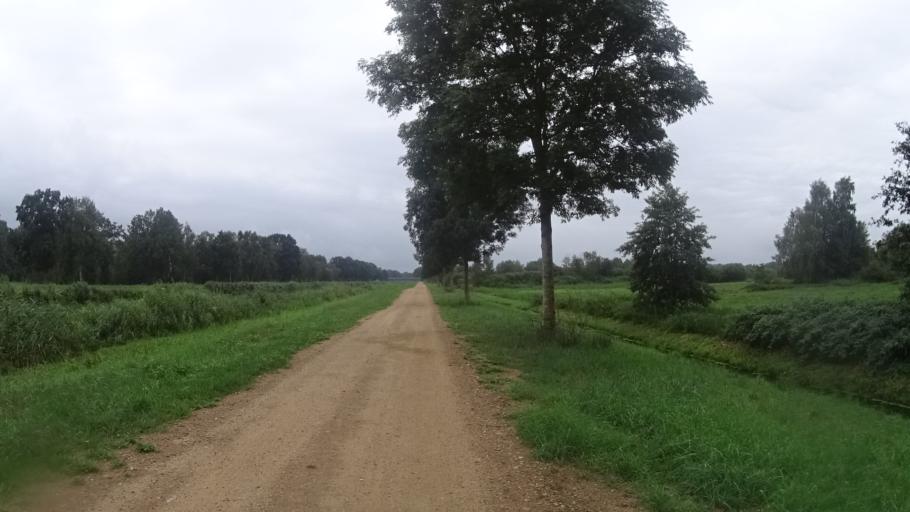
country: DE
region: Schleswig-Holstein
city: Buchen
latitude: 53.4871
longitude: 10.6303
